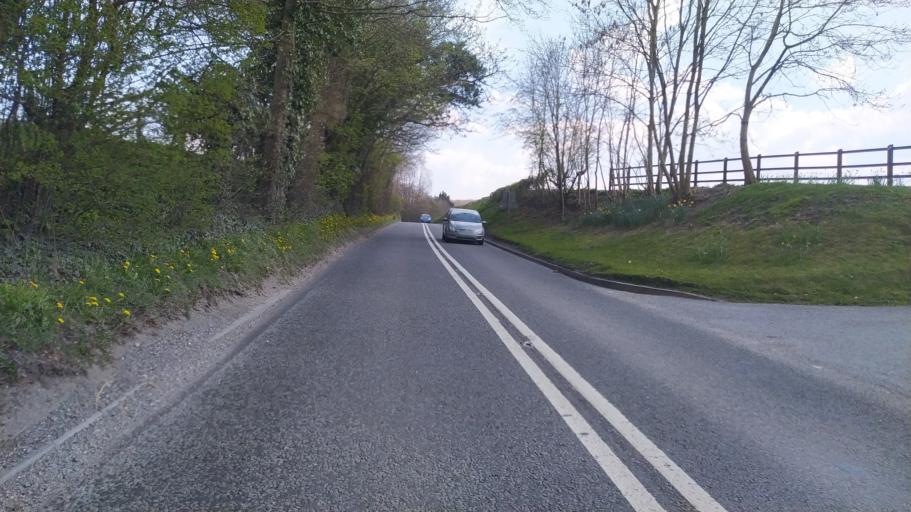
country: GB
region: England
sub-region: Wiltshire
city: Corsley
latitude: 51.2056
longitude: -2.2459
